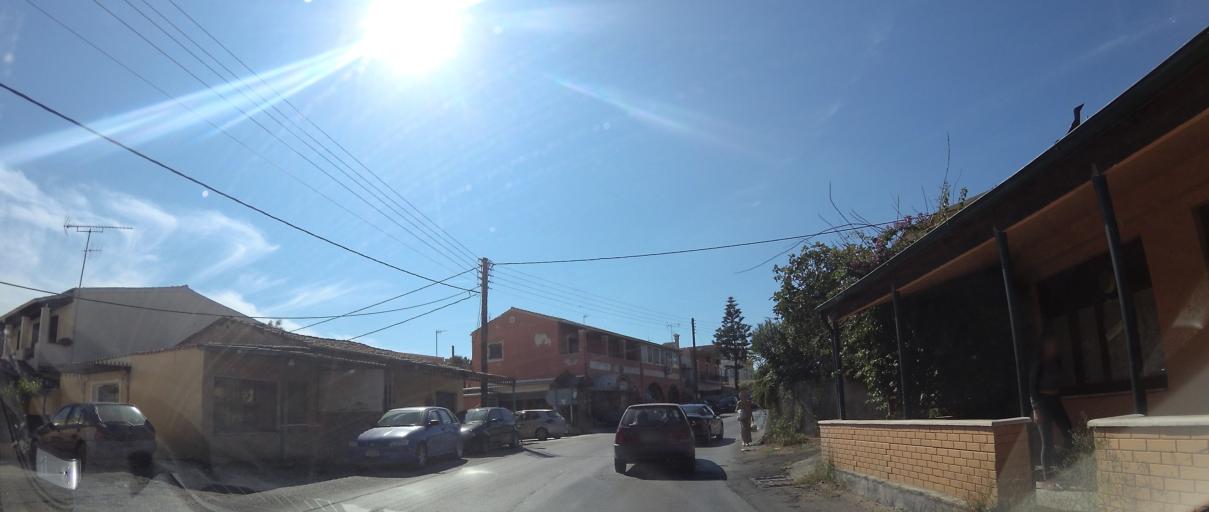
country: GR
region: Ionian Islands
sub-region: Nomos Kerkyras
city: Alepou
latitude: 39.6136
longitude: 19.8897
